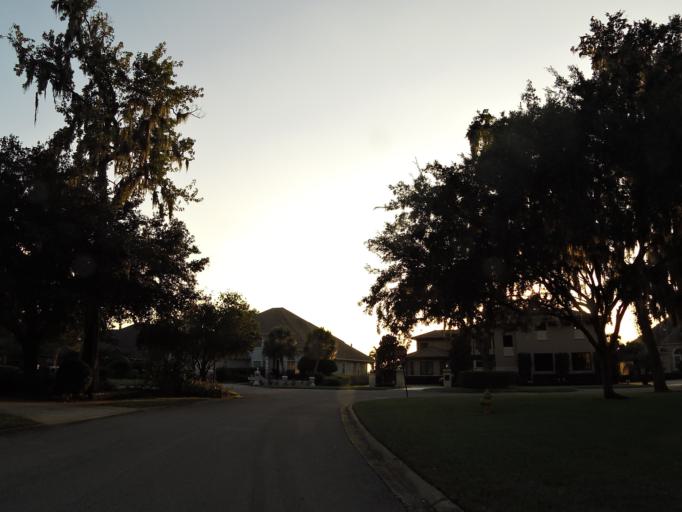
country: US
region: Florida
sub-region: Clay County
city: Orange Park
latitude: 30.1793
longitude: -81.6421
